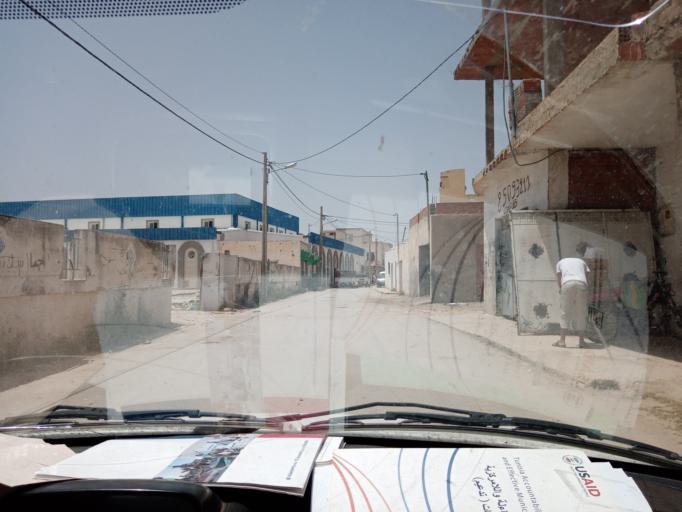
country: TN
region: Al Qayrawan
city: Sbikha
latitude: 36.1171
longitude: 10.0976
